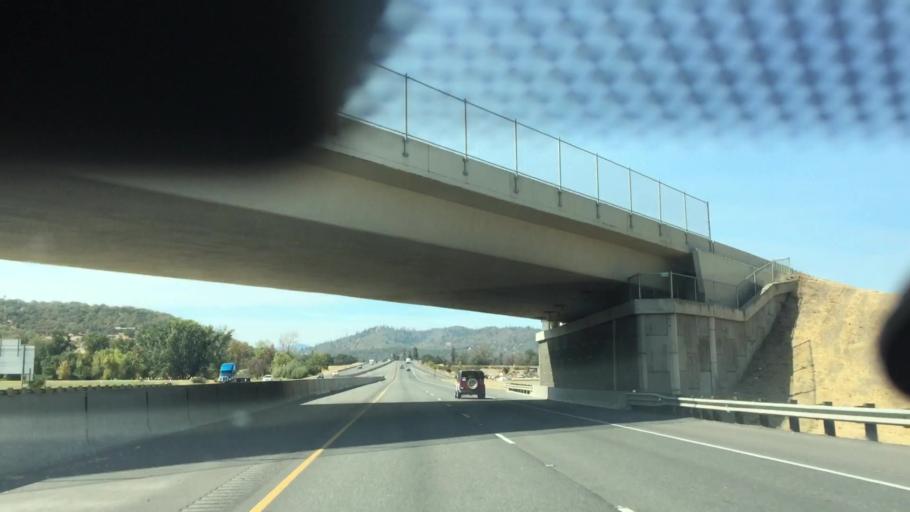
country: US
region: Oregon
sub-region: Jackson County
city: Central Point
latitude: 42.4071
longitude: -122.9424
